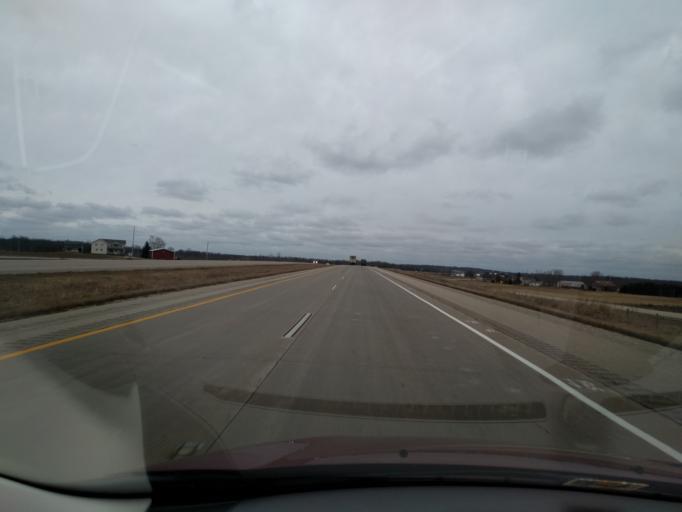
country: US
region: Wisconsin
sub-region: Winnebago County
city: Winneconne
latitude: 44.2271
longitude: -88.7115
